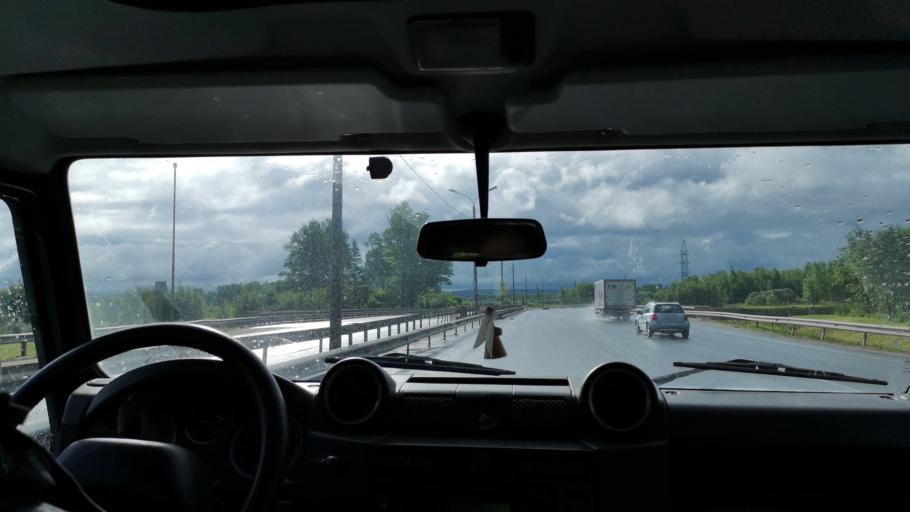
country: RU
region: Moskovskaya
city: Dmitrov
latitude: 56.3653
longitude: 37.4729
